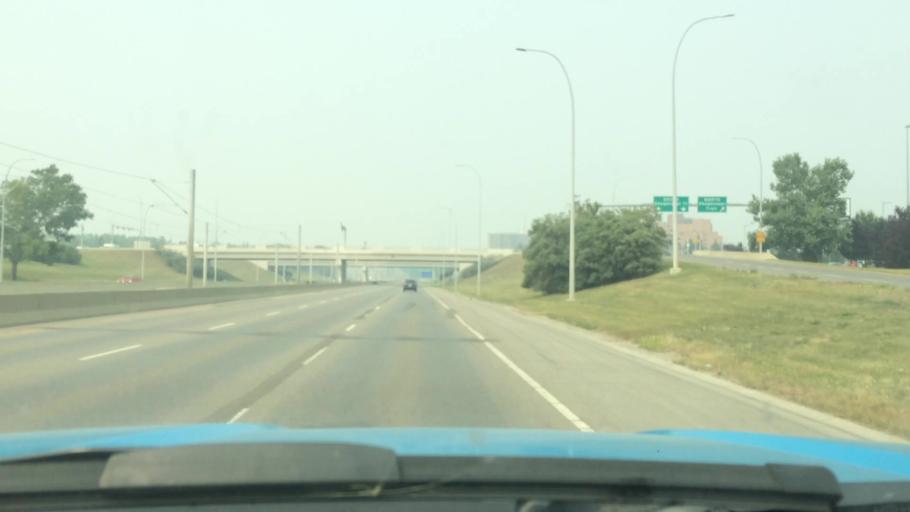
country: CA
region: Alberta
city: Calgary
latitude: 51.0965
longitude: -114.1464
